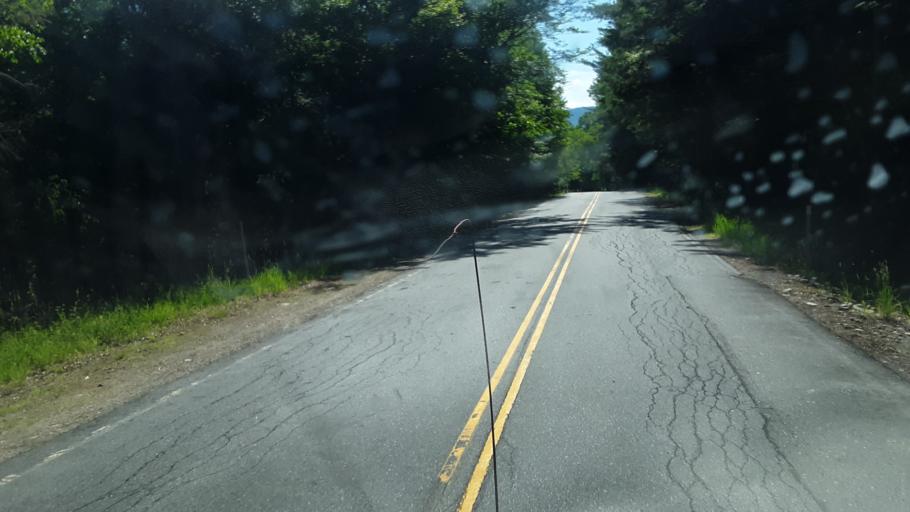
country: US
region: New Hampshire
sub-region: Grafton County
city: North Haverhill
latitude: 44.0981
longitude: -71.8632
